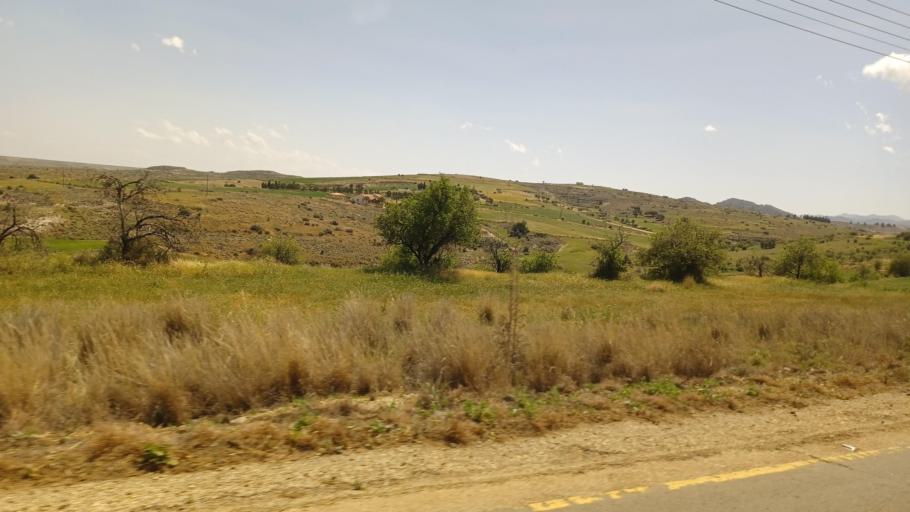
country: CY
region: Lefkosia
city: Astromeritis
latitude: 35.0880
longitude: 33.0144
